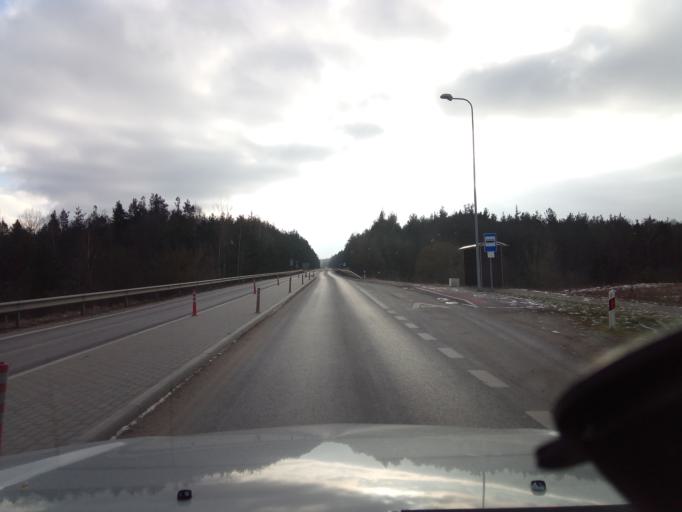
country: LT
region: Alytaus apskritis
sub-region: Alytaus rajonas
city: Daugai
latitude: 54.1682
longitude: 24.2085
